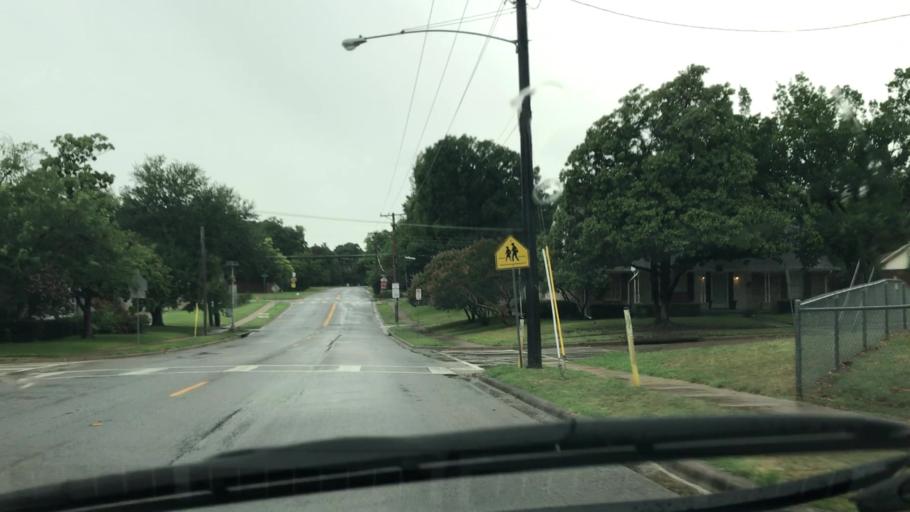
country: US
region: Texas
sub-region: Dallas County
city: Richardson
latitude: 32.9339
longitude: -96.7772
